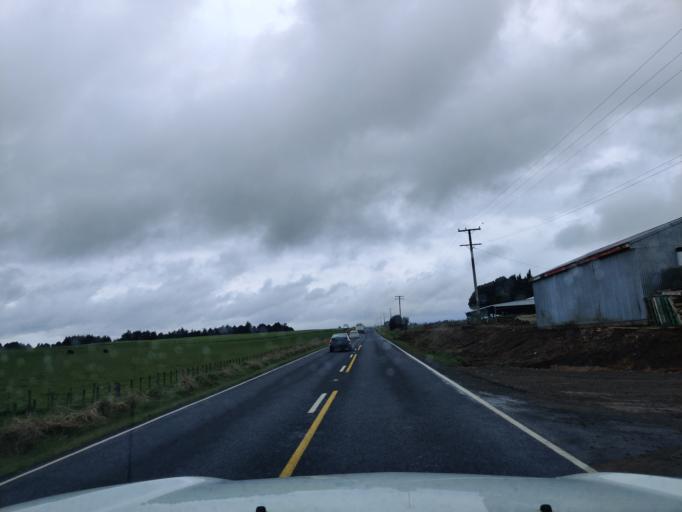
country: NZ
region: Manawatu-Wanganui
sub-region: Ruapehu District
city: Waiouru
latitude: -39.3600
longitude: 175.3479
